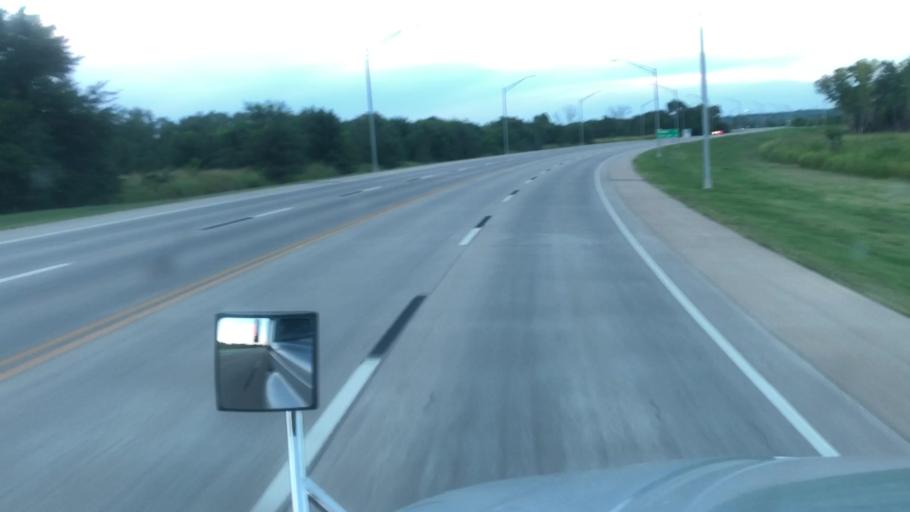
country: US
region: Oklahoma
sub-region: Kay County
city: Ponca City
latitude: 36.6841
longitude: -97.0699
